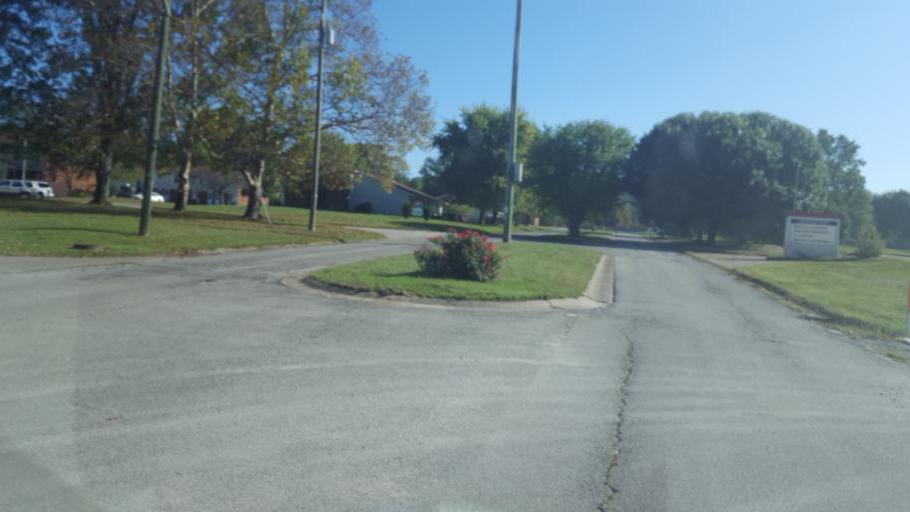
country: US
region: Ohio
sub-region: Brown County
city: Aberdeen
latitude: 38.6738
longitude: -83.7725
